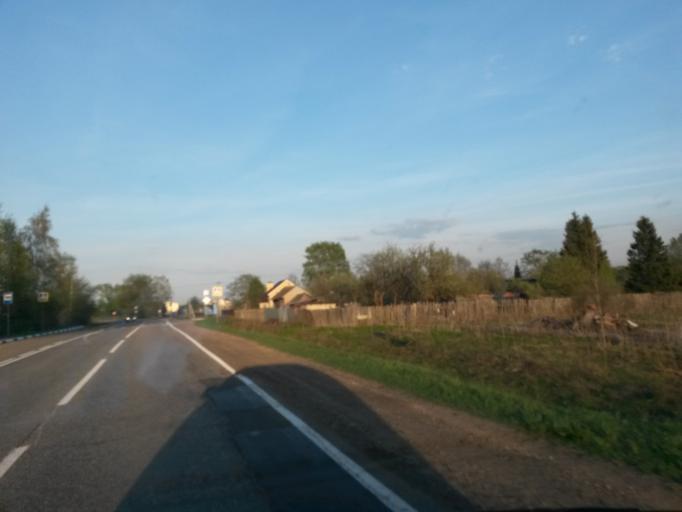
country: RU
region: Jaroslavl
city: Konstantinovskiy
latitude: 57.6683
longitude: 39.6372
